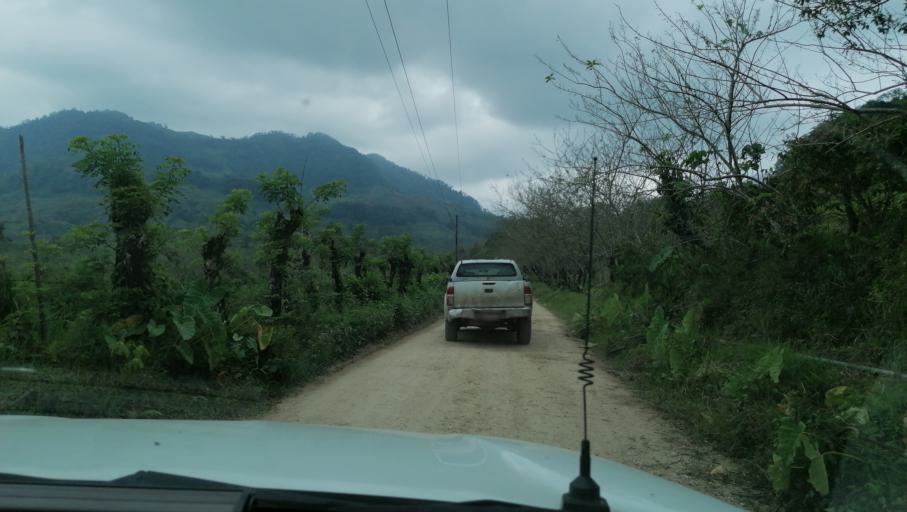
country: MX
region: Chiapas
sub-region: Ocotepec
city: San Pablo Huacano
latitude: 17.2672
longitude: -93.2528
